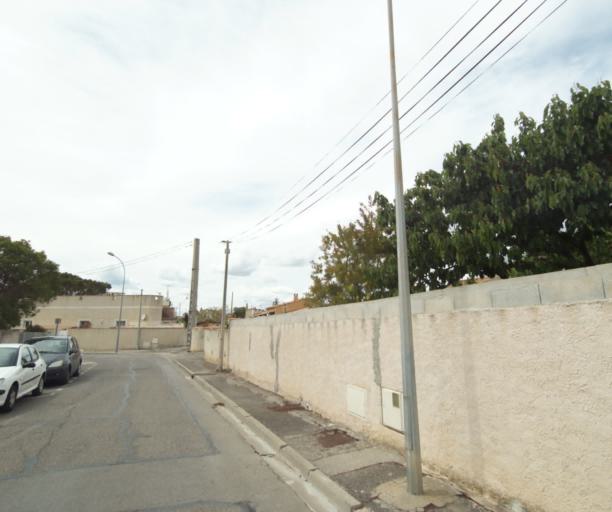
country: FR
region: Provence-Alpes-Cote d'Azur
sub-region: Departement des Bouches-du-Rhone
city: Rognac
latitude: 43.4864
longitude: 5.2357
